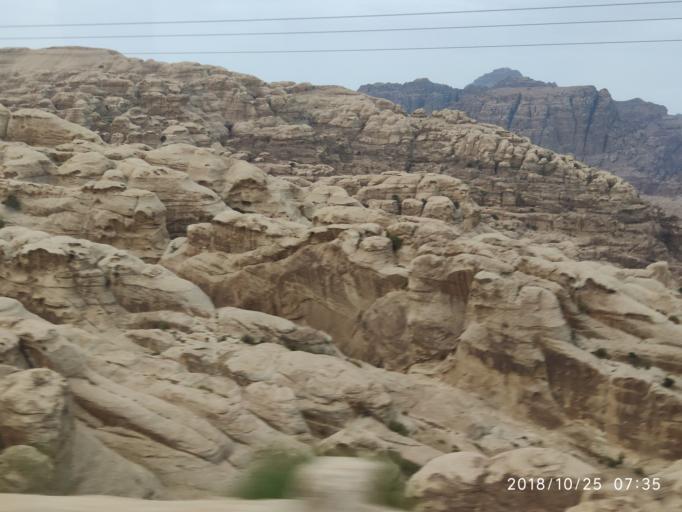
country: JO
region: Ma'an
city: Petra
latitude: 30.3364
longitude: 35.4678
